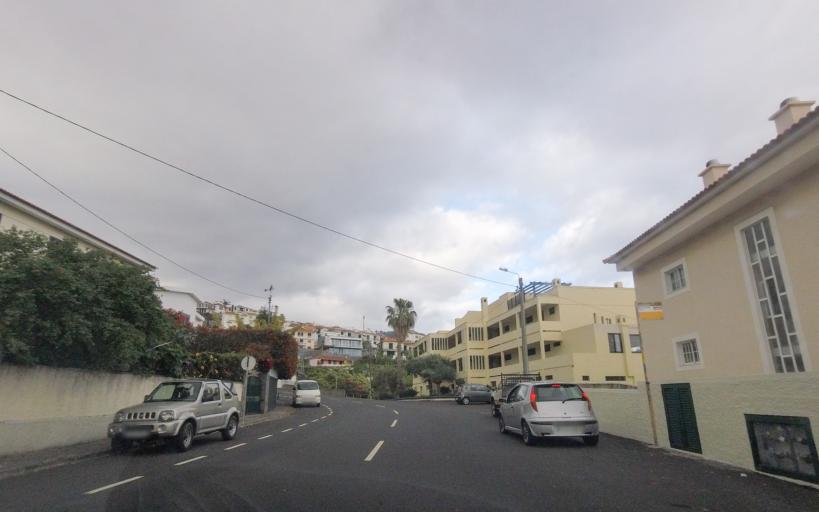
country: PT
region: Madeira
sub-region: Funchal
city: Nossa Senhora do Monte
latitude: 32.6542
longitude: -16.8977
